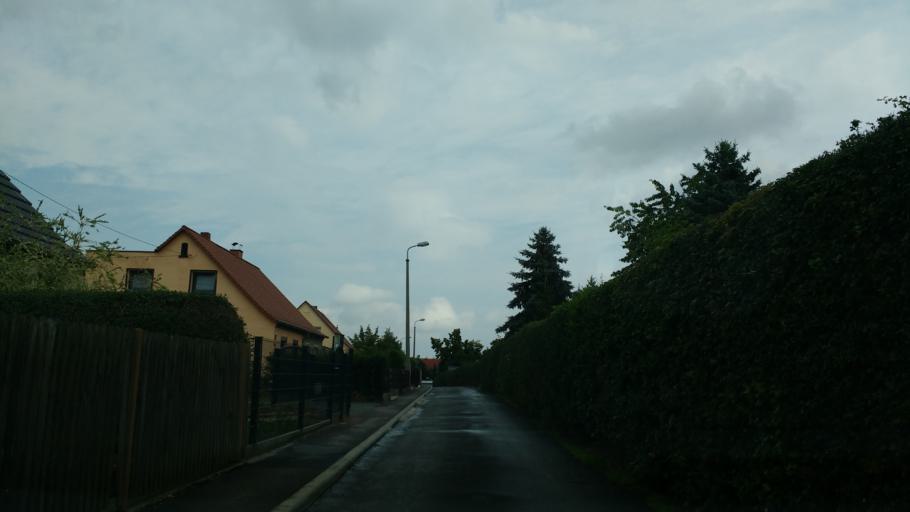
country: DE
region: Saxony-Anhalt
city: Zeitz
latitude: 51.0398
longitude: 12.1288
